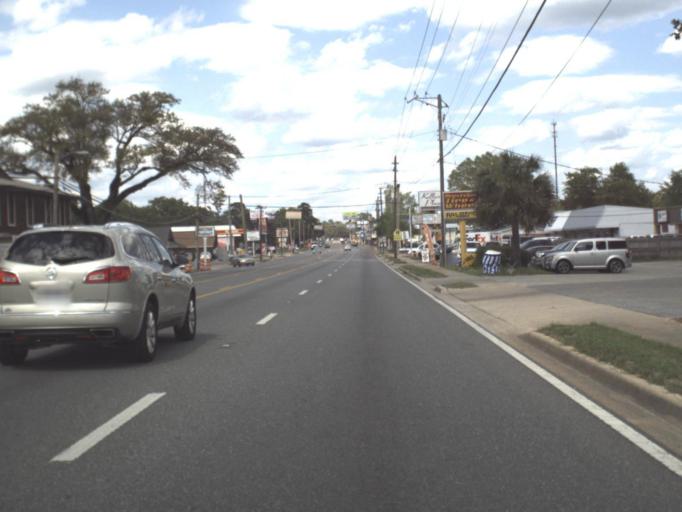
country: US
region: Florida
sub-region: Okaloosa County
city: Crestview
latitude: 30.7674
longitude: -86.5677
